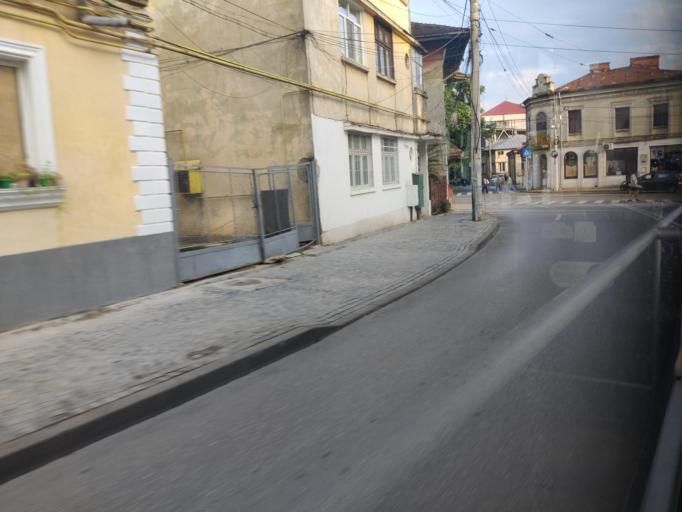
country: RO
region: Iasi
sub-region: Municipiul Iasi
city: Iasi
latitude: 47.1642
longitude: 27.5880
